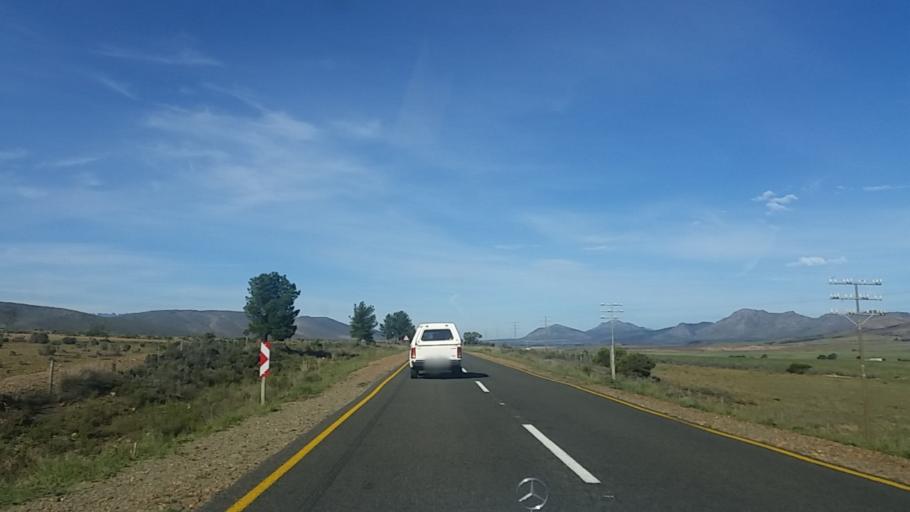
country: ZA
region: Western Cape
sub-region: Eden District Municipality
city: George
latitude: -33.8186
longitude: 22.5027
